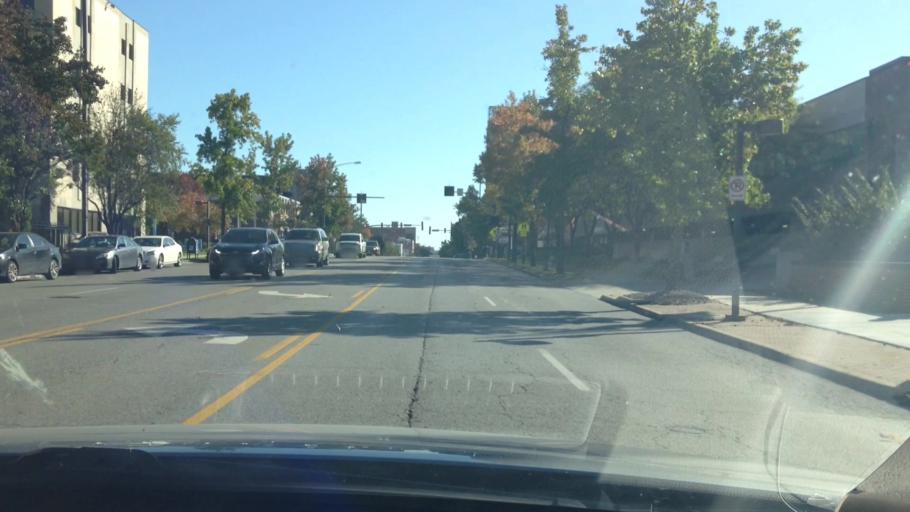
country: US
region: Missouri
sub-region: Jackson County
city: Kansas City
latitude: 39.0694
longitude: -94.5901
